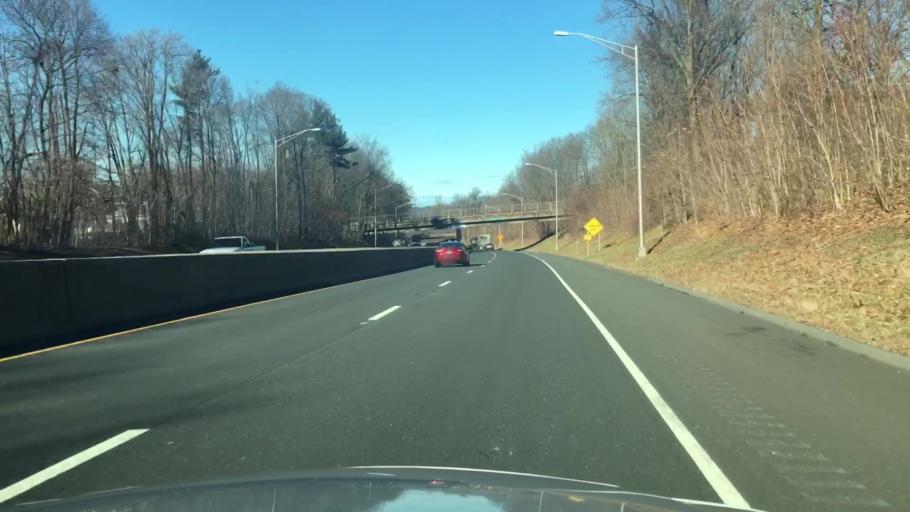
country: US
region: Connecticut
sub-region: Middlesex County
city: Middletown
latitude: 41.5494
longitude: -72.6314
